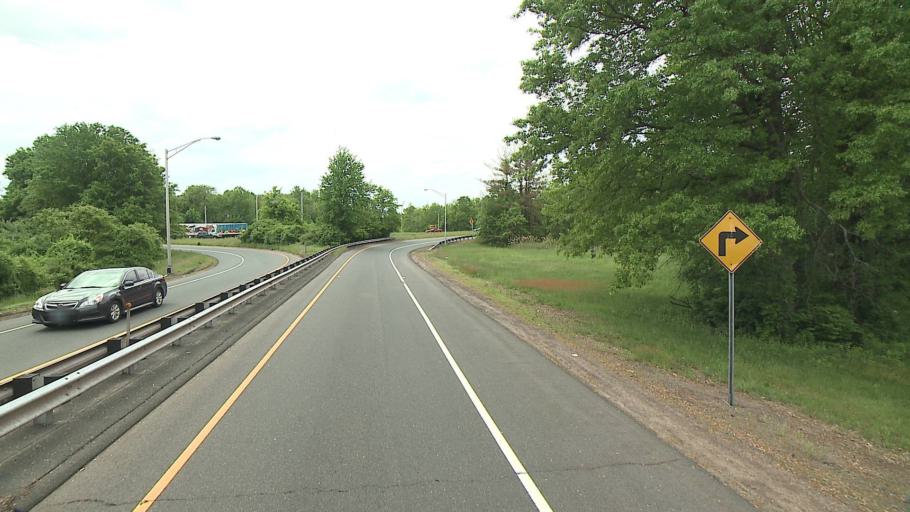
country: US
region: Connecticut
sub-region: Hartford County
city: Thompsonville
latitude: 41.9911
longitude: -72.5857
